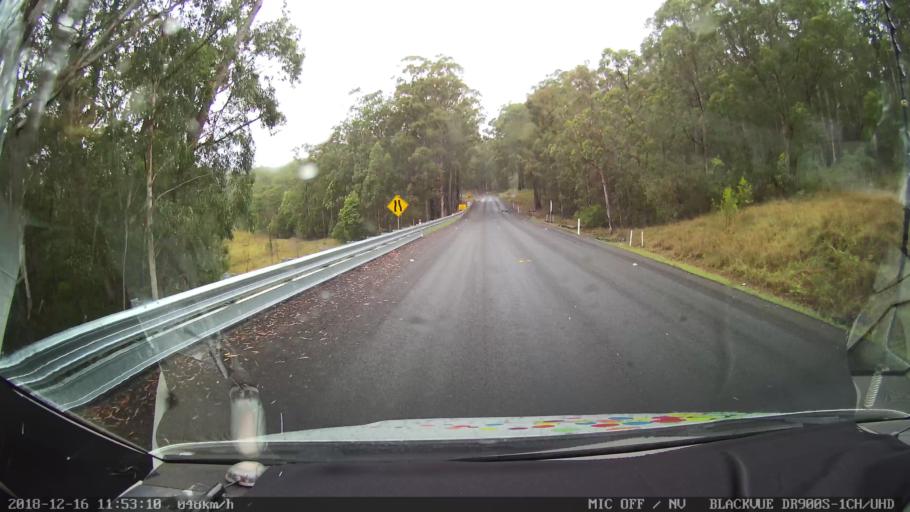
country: AU
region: New South Wales
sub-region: Tenterfield Municipality
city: Carrolls Creek
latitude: -28.9037
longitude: 152.2777
